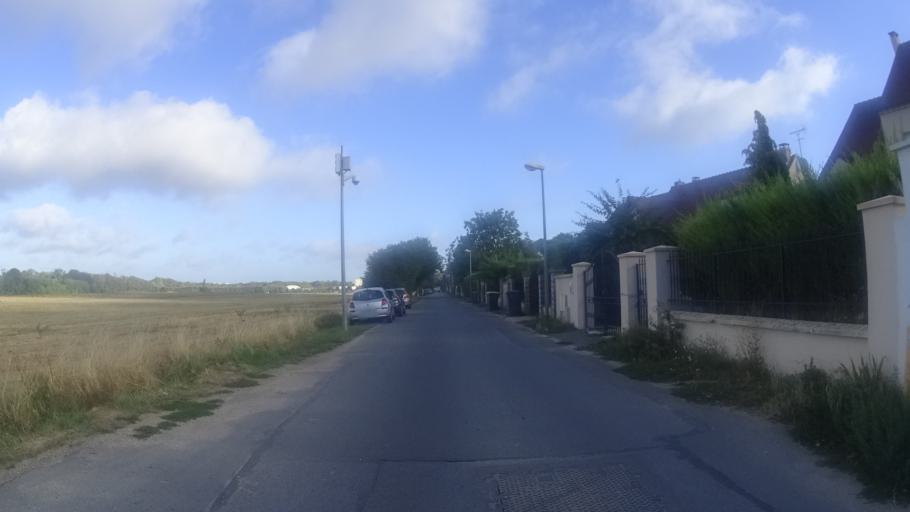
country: FR
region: Ile-de-France
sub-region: Departement de l'Essonne
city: Ris-Orangis
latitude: 48.6674
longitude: 2.4139
